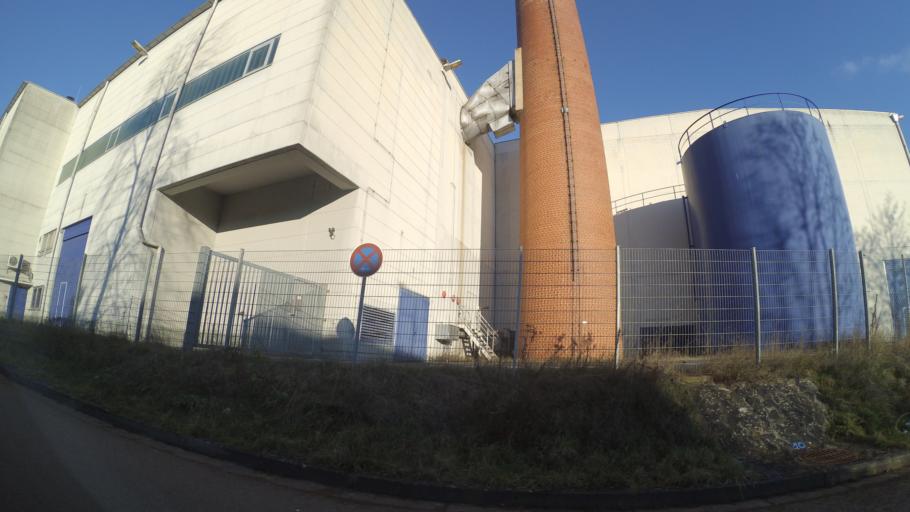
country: DE
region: Saarland
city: Heusweiler
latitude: 49.3642
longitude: 6.9281
